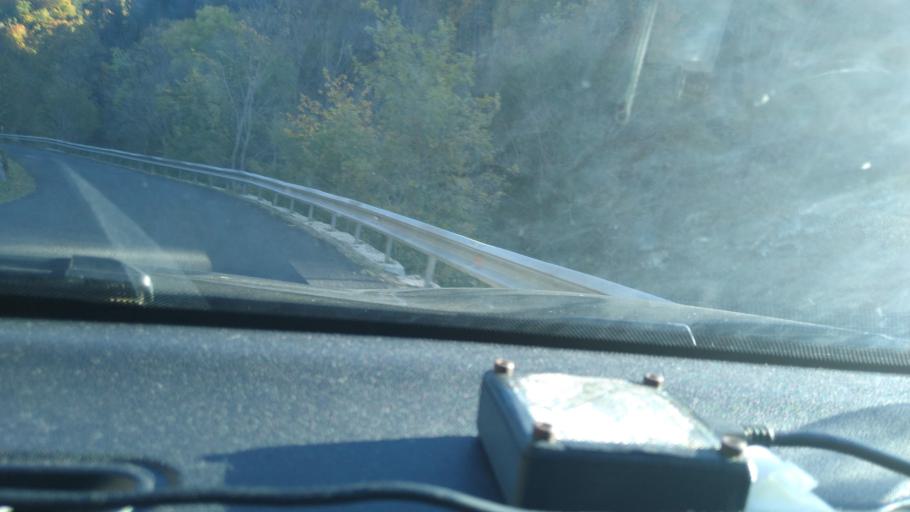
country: FR
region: Languedoc-Roussillon
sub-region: Departement de l'Aude
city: Quillan
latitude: 42.7375
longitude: 2.2073
